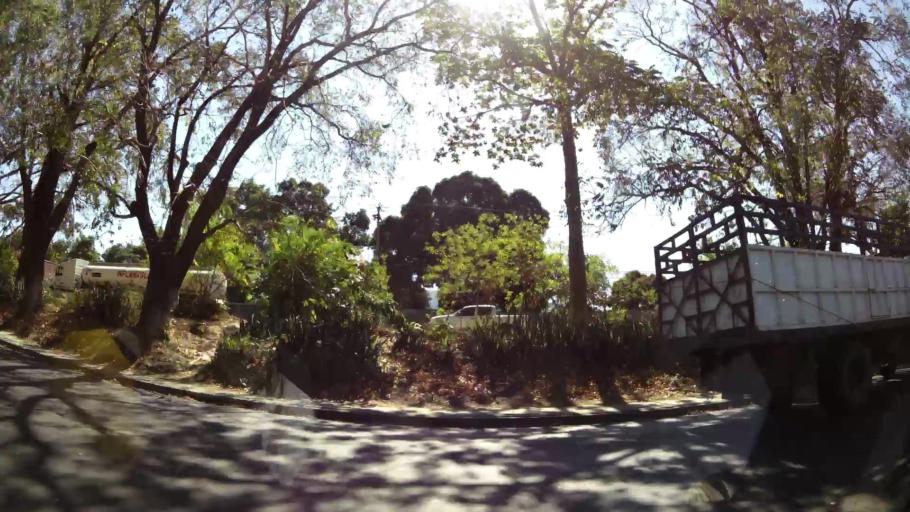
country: SV
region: La Libertad
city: Santa Tecla
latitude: 13.7263
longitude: -89.3749
